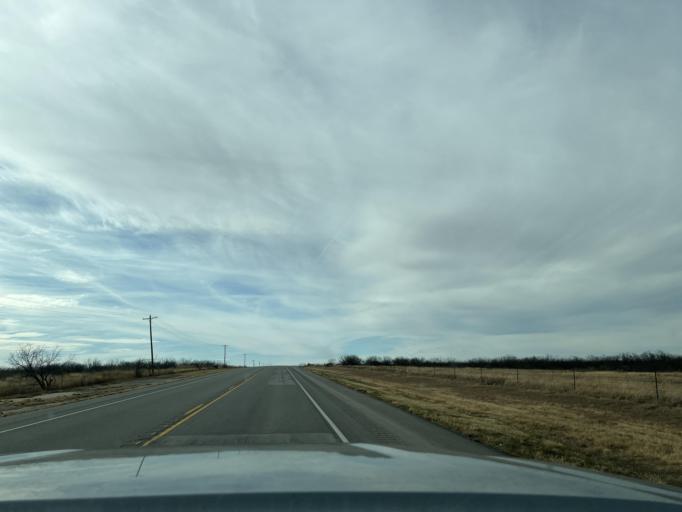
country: US
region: Texas
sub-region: Jones County
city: Anson
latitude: 32.7505
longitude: -99.6673
